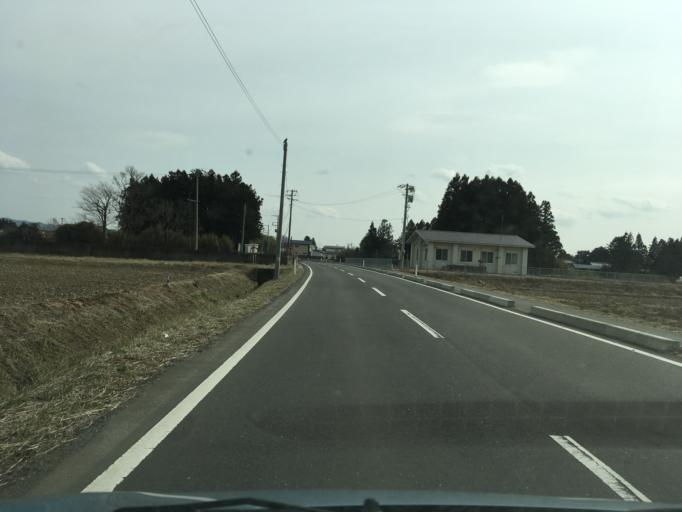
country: JP
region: Miyagi
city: Wakuya
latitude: 38.7220
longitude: 141.2407
